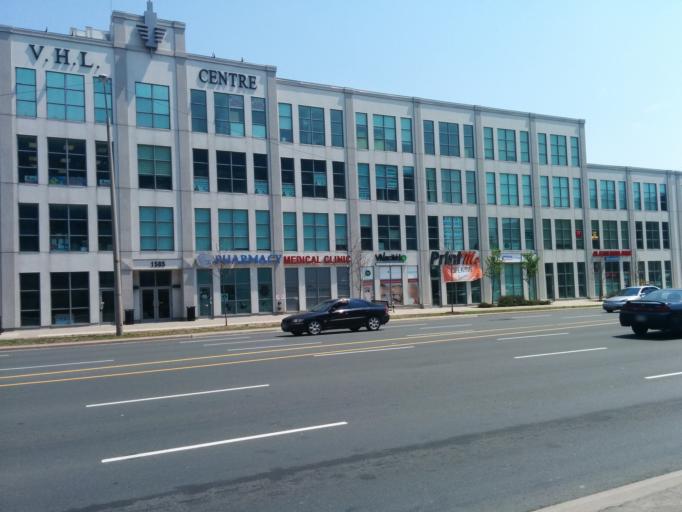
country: CA
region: Ontario
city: Scarborough
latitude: 43.7921
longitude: -79.2383
